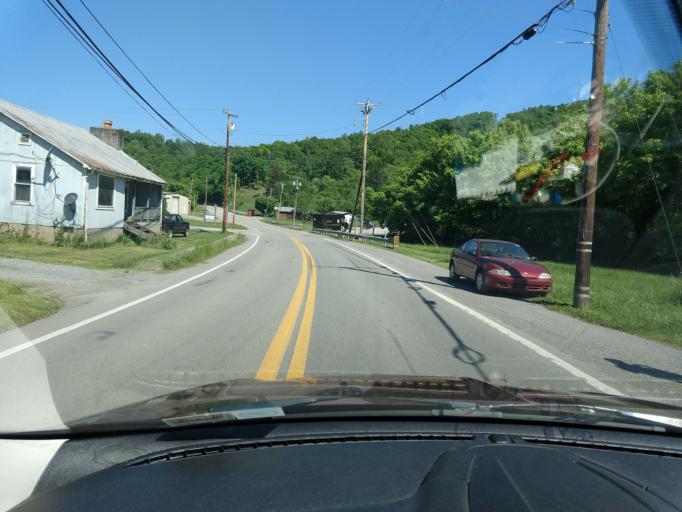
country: US
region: West Virginia
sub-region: Gilmer County
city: Glenville
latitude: 38.9144
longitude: -80.7496
